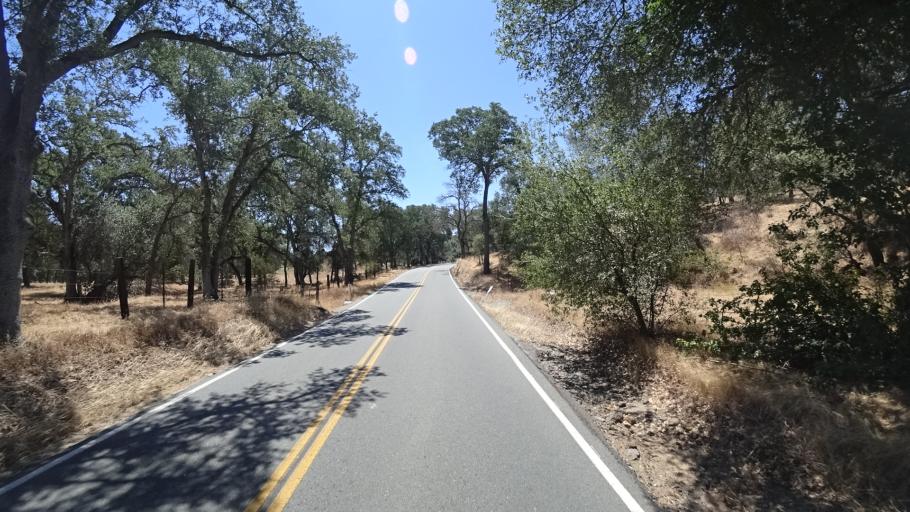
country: US
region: California
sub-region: Calaveras County
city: Rancho Calaveras
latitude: 38.1364
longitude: -120.8806
